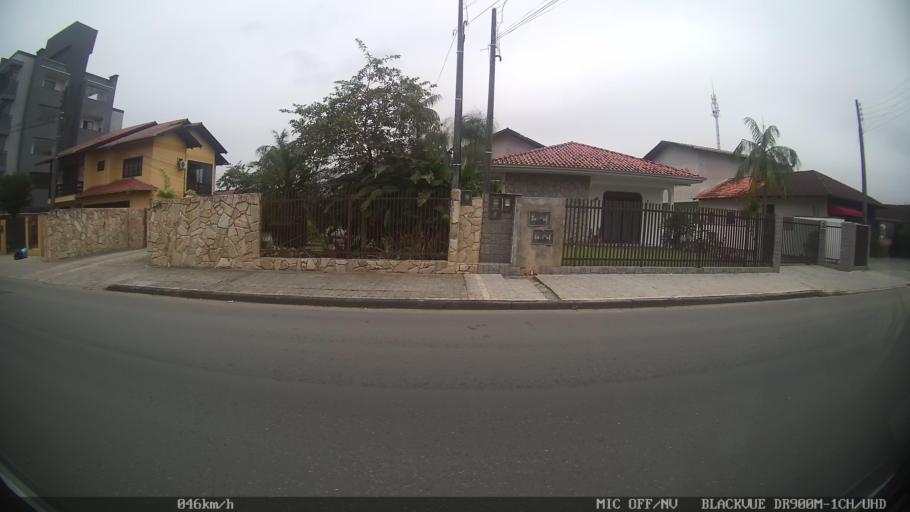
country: BR
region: Santa Catarina
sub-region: Joinville
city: Joinville
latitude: -26.2663
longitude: -48.8169
